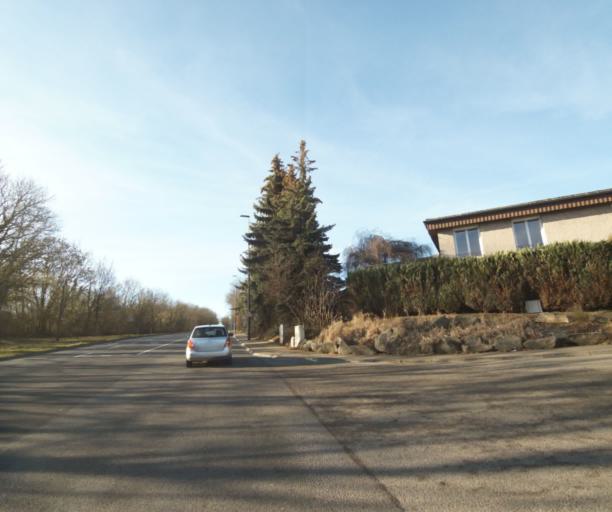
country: FR
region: Lorraine
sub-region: Departement de Meurthe-et-Moselle
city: Villers-les-Nancy
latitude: 48.6621
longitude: 6.1420
